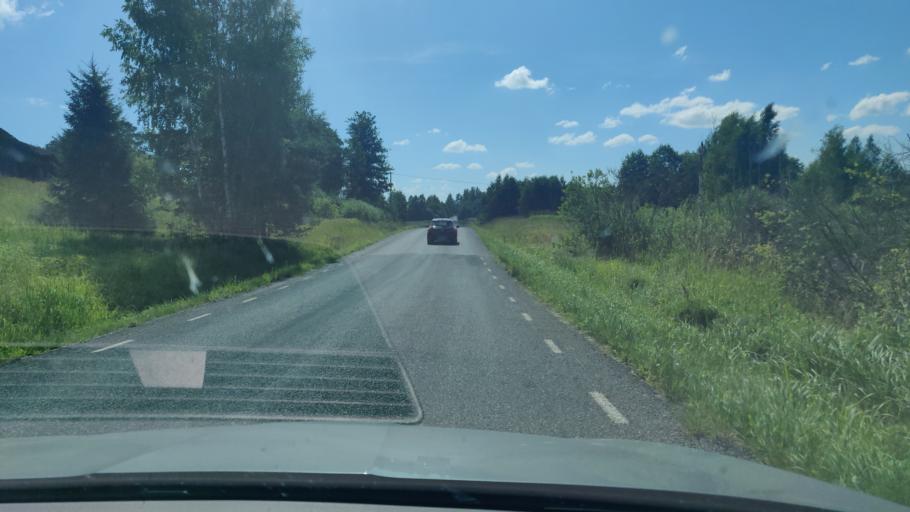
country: EE
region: Tartu
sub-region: Elva linn
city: Elva
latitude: 58.1466
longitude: 26.4747
